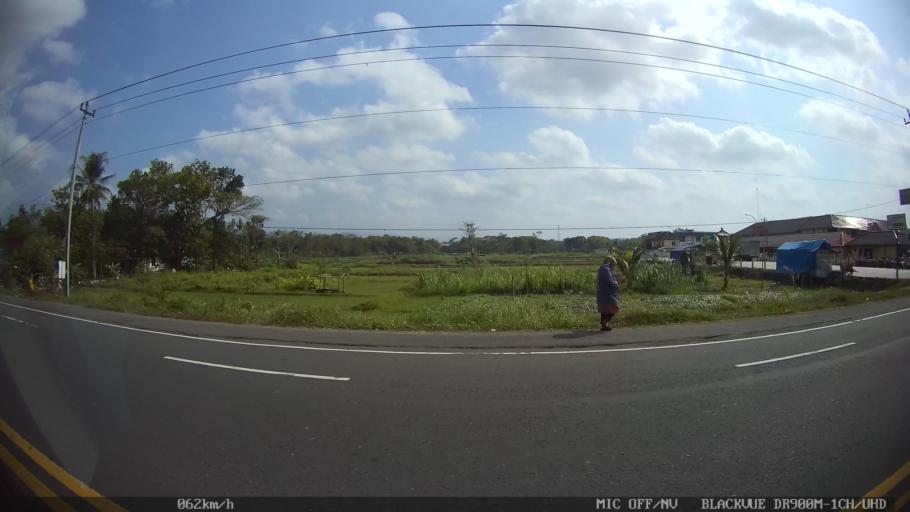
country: ID
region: Daerah Istimewa Yogyakarta
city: Srandakan
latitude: -7.8669
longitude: 110.1749
